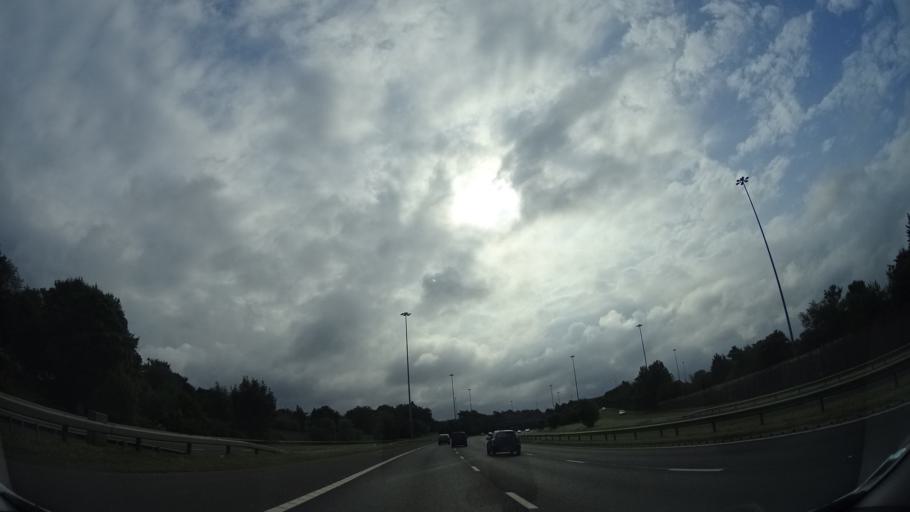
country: GB
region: England
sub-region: Knowsley
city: Huyton
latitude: 53.4085
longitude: -2.8740
